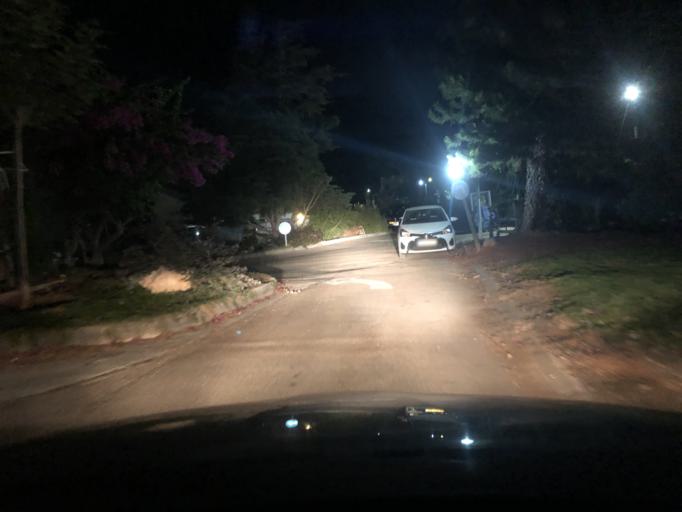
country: IL
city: Nirit
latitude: 32.1353
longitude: 34.9702
